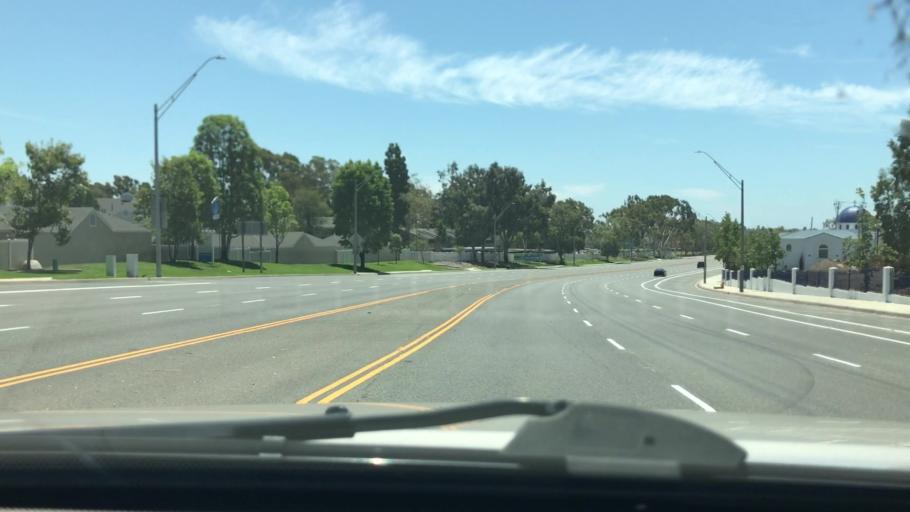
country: US
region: California
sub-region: Orange County
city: Seal Beach
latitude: 33.7728
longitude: -118.1193
